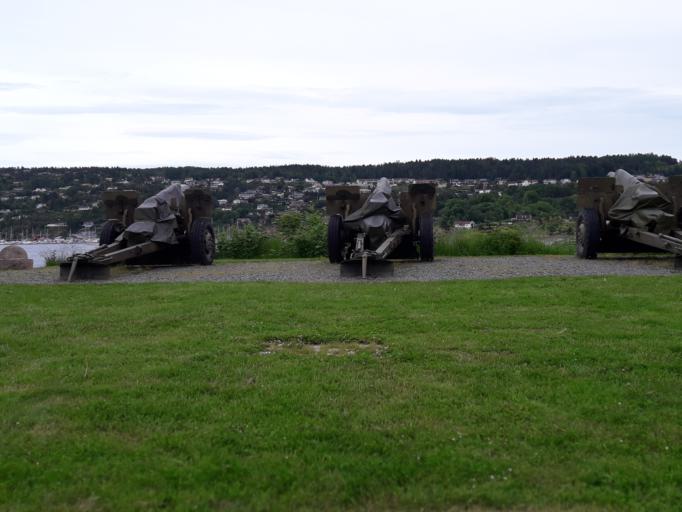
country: NO
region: Akershus
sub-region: Frogn
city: Drobak
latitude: 59.6738
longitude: 10.6083
